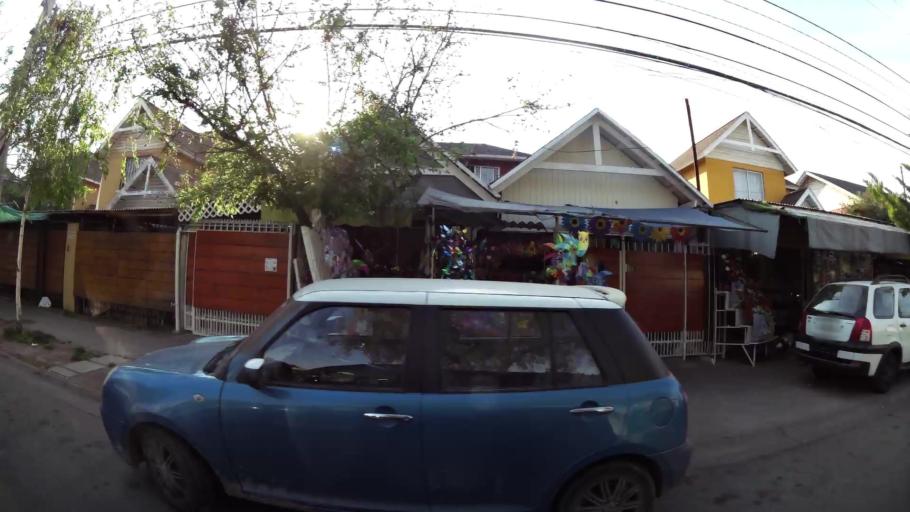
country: CL
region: Santiago Metropolitan
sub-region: Provincia de Cordillera
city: Puente Alto
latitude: -33.5595
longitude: -70.5480
